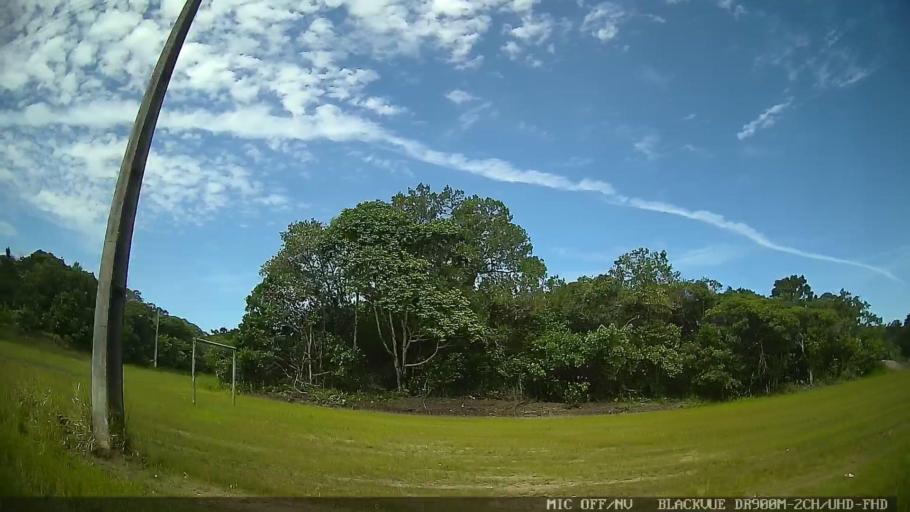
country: BR
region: Sao Paulo
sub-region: Iguape
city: Iguape
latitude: -24.7176
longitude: -47.5225
